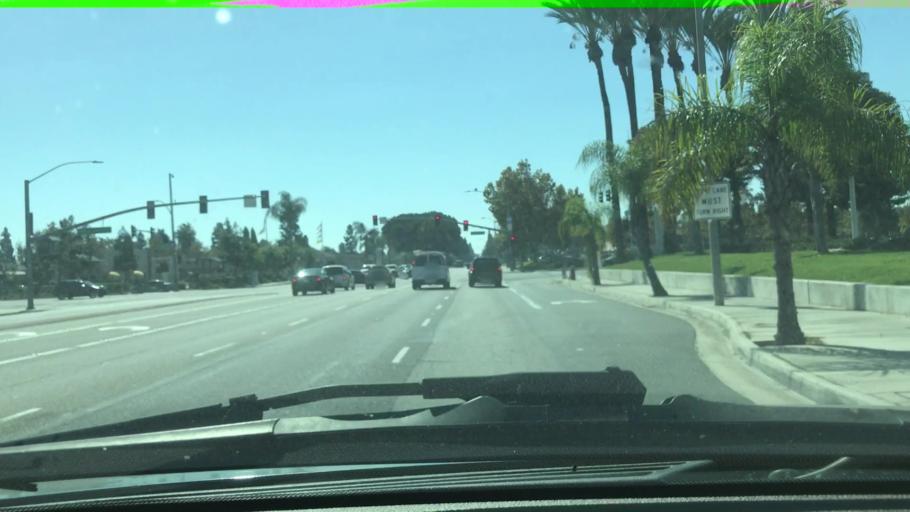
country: US
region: California
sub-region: Orange County
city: Fountain Valley
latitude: 33.7007
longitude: -117.9078
